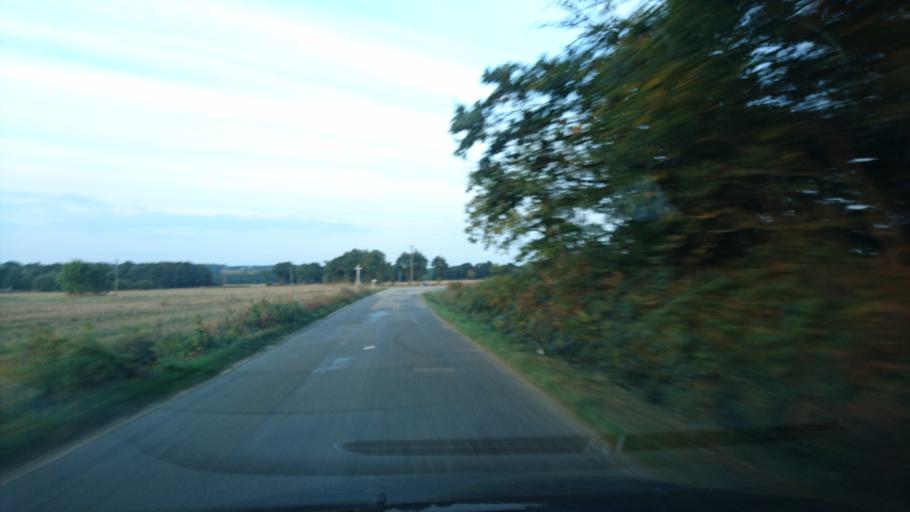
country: FR
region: Brittany
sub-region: Departement du Morbihan
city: Guer
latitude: 47.8876
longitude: -2.0598
